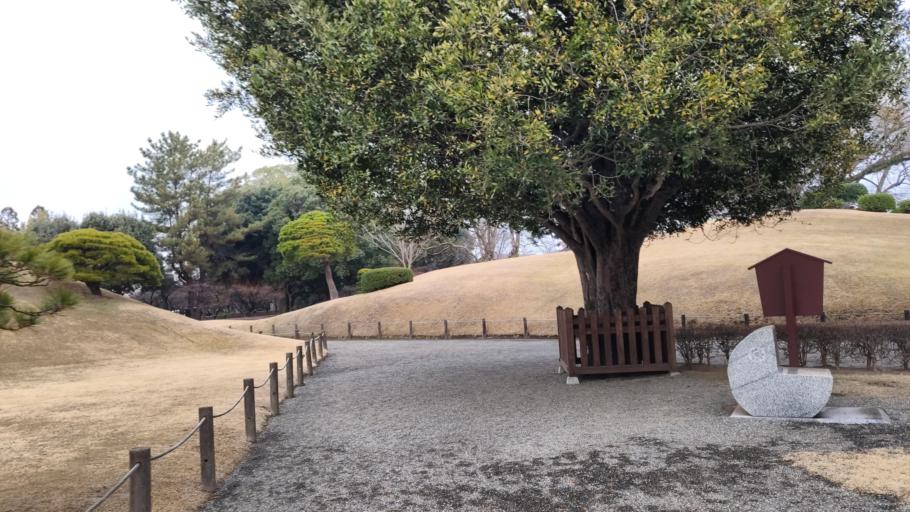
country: JP
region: Kumamoto
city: Kumamoto
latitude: 32.7911
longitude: 130.7356
